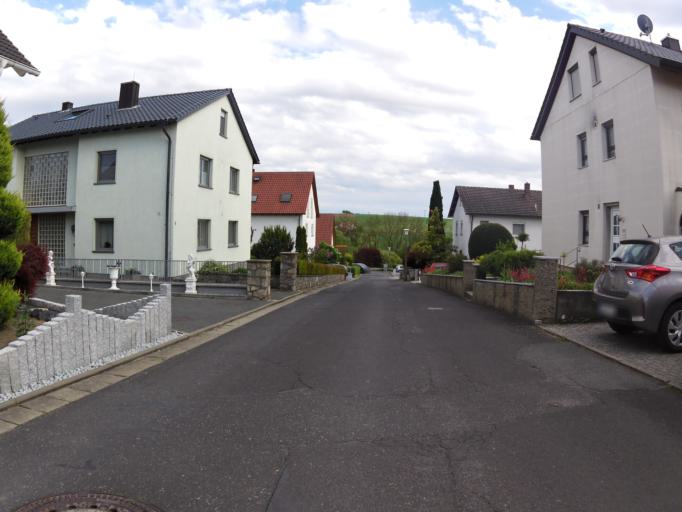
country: DE
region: Bavaria
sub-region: Regierungsbezirk Unterfranken
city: Kurnach
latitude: 49.8456
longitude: 10.0350
